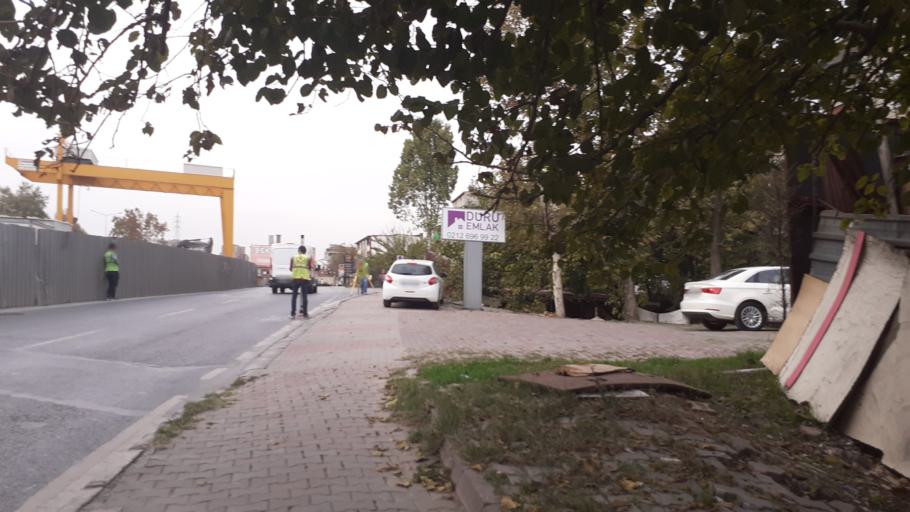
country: TR
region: Istanbul
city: Mahmutbey
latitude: 41.0472
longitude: 28.8021
